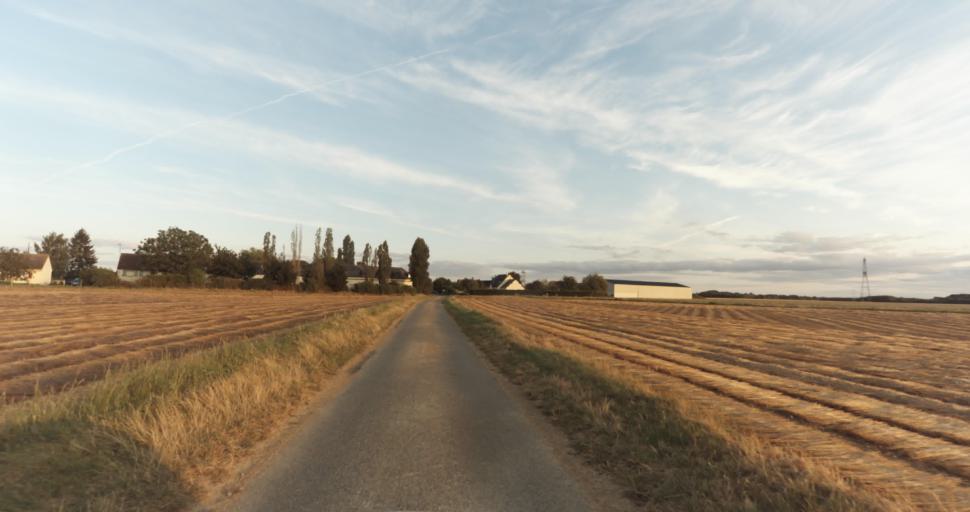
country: FR
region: Haute-Normandie
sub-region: Departement de l'Eure
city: La Madeleine-de-Nonancourt
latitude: 48.8550
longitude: 1.2133
